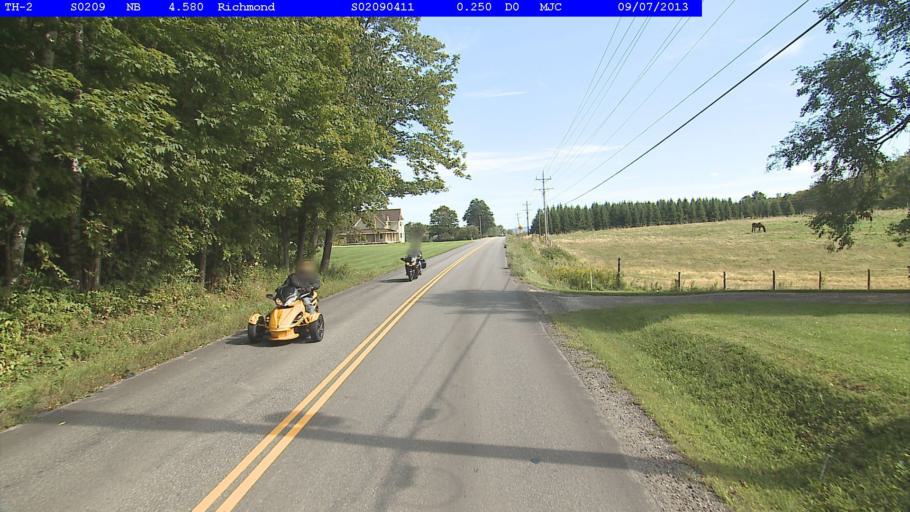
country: US
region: Vermont
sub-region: Chittenden County
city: Williston
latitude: 44.3749
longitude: -73.0630
